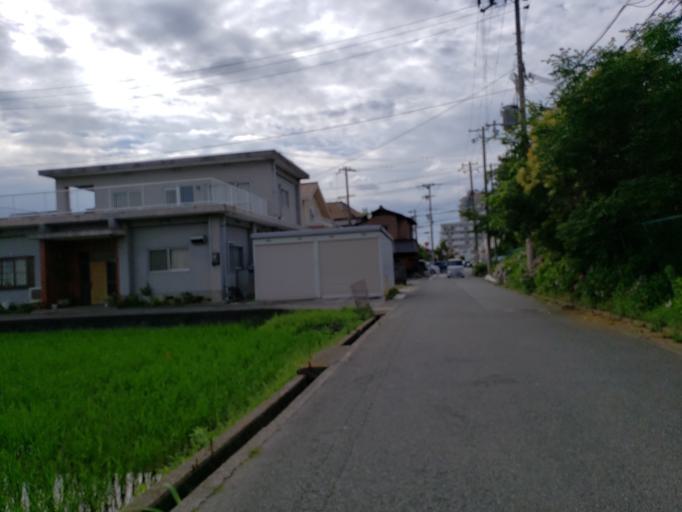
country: JP
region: Hyogo
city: Kakogawacho-honmachi
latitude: 34.7664
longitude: 134.8224
